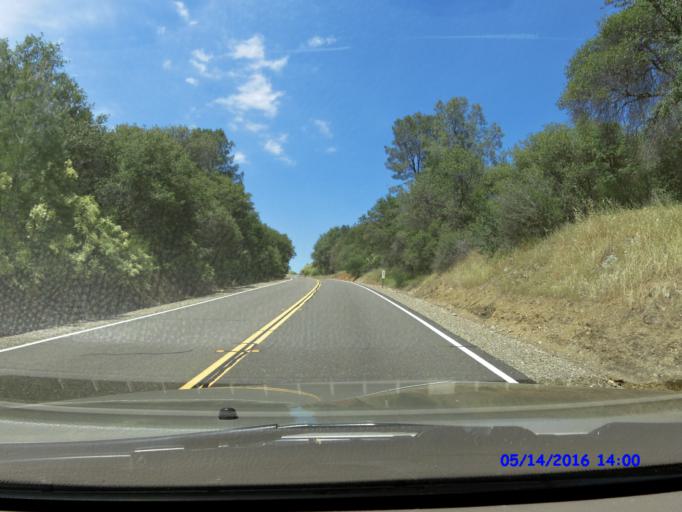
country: US
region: California
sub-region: Mariposa County
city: Mariposa
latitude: 37.5804
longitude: -120.1201
